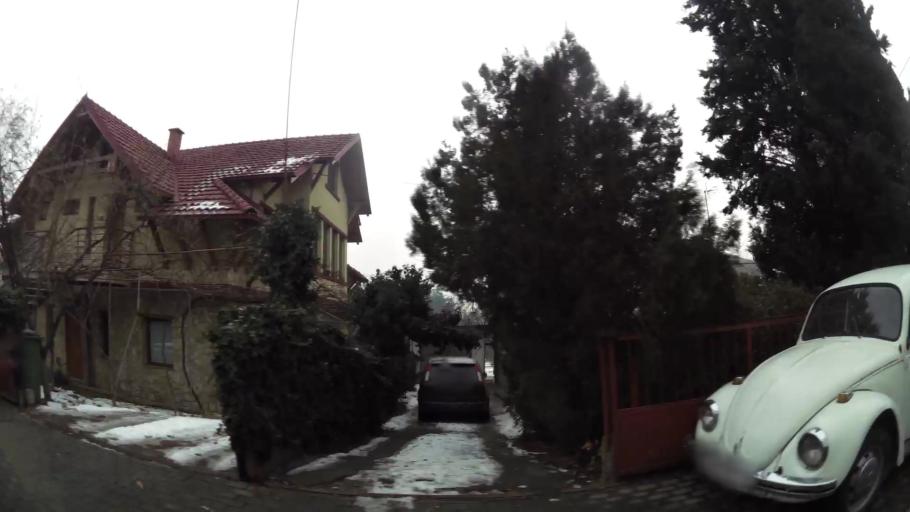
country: MK
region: Cair
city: Cair
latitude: 42.0151
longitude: 21.4565
